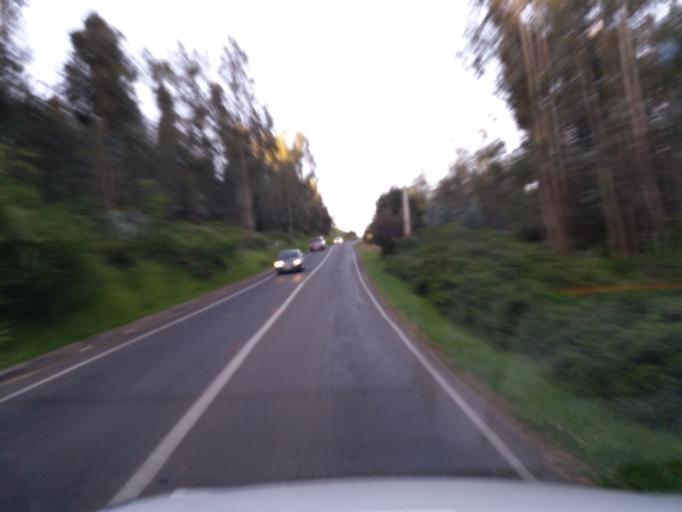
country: CL
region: Valparaiso
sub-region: Provincia de Quillota
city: Quillota
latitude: -32.8849
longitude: -71.2789
